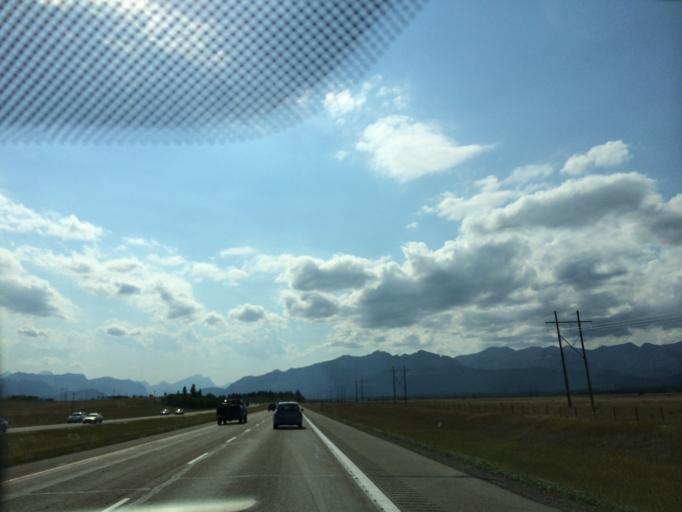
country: CA
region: Alberta
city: Canmore
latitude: 51.1300
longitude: -114.9492
